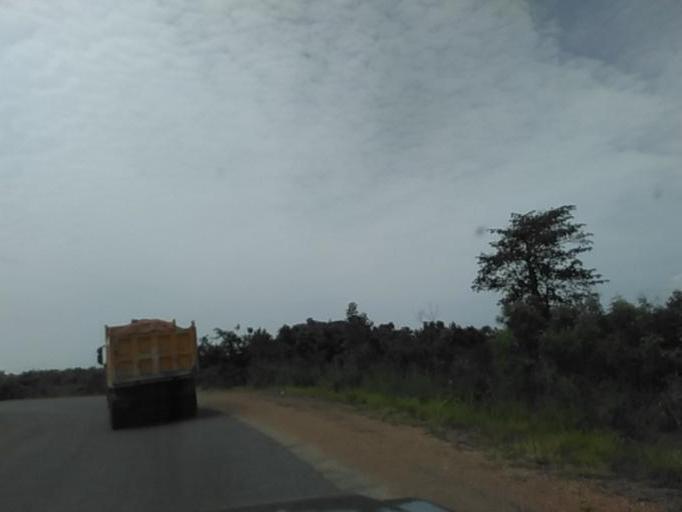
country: GH
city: Akropong
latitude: 6.0936
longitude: 0.0617
